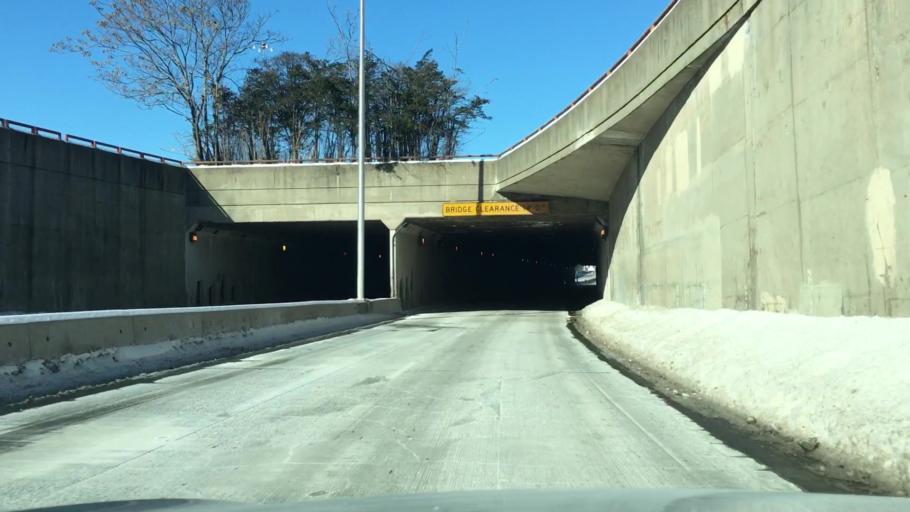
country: US
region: Massachusetts
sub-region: Hampden County
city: West Springfield
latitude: 42.1069
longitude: -72.6151
